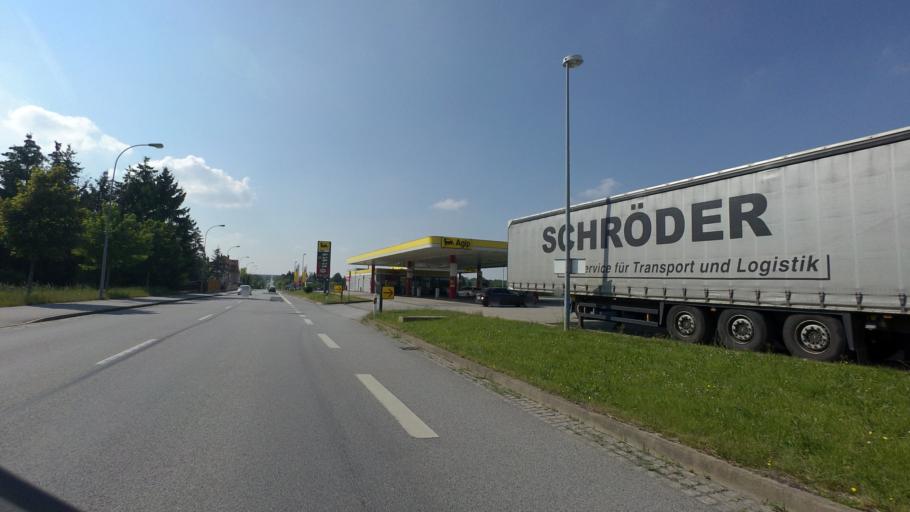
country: DE
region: Saxony
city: Kubschutz
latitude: 51.1722
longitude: 14.4757
